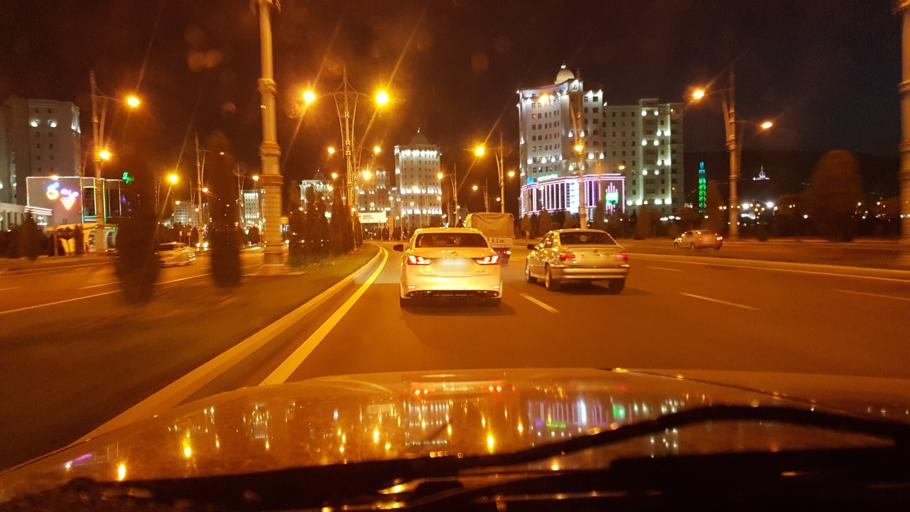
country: TM
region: Ahal
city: Ashgabat
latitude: 37.9083
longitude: 58.3379
